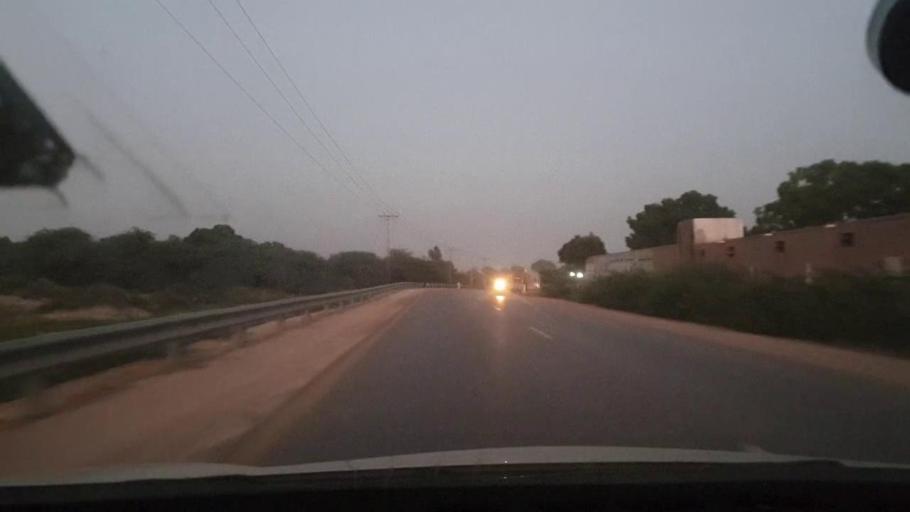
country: PK
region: Sindh
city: Tando Adam
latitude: 25.7475
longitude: 68.6544
